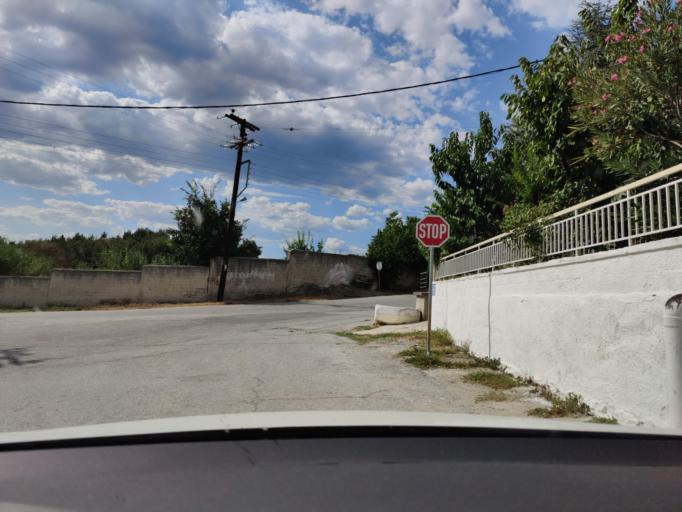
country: GR
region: Central Macedonia
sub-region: Nomos Serron
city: Serres
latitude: 41.0901
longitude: 23.5350
